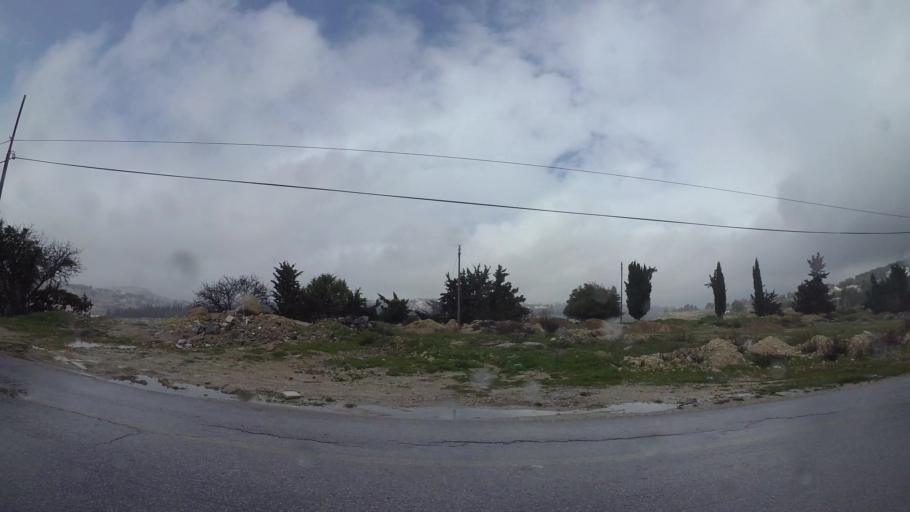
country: JO
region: Amman
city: Al Jubayhah
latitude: 32.0142
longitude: 35.8063
